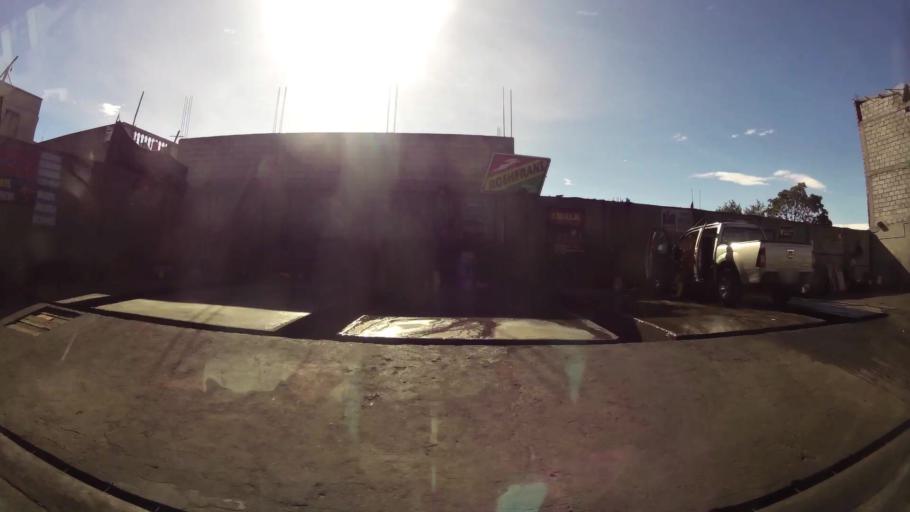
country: EC
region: Pichincha
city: Quito
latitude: -0.3164
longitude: -78.5580
